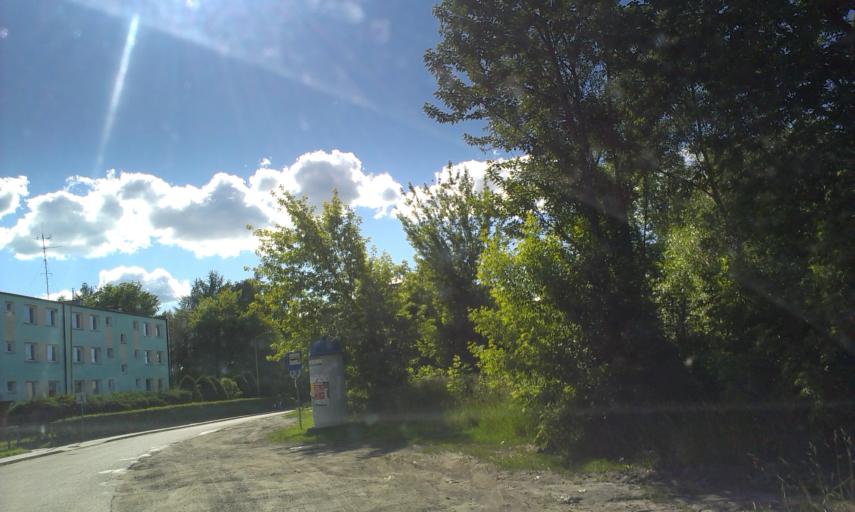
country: PL
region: West Pomeranian Voivodeship
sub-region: Powiat szczecinecki
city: Szczecinek
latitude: 53.6857
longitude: 16.6844
